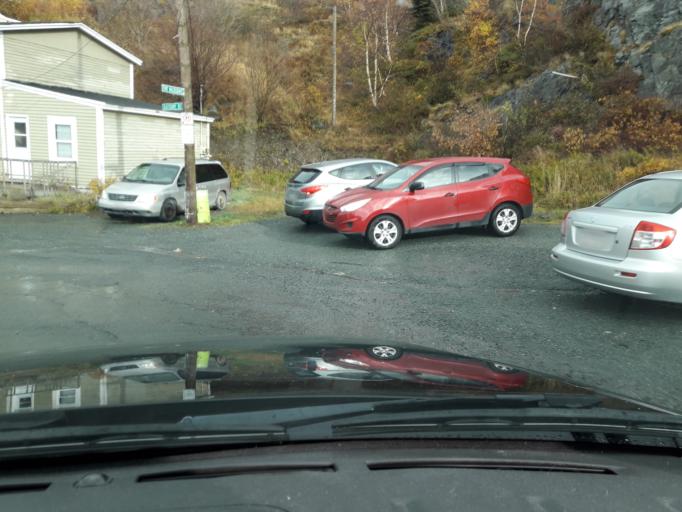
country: CA
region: Newfoundland and Labrador
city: St. John's
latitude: 47.5696
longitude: -52.6907
